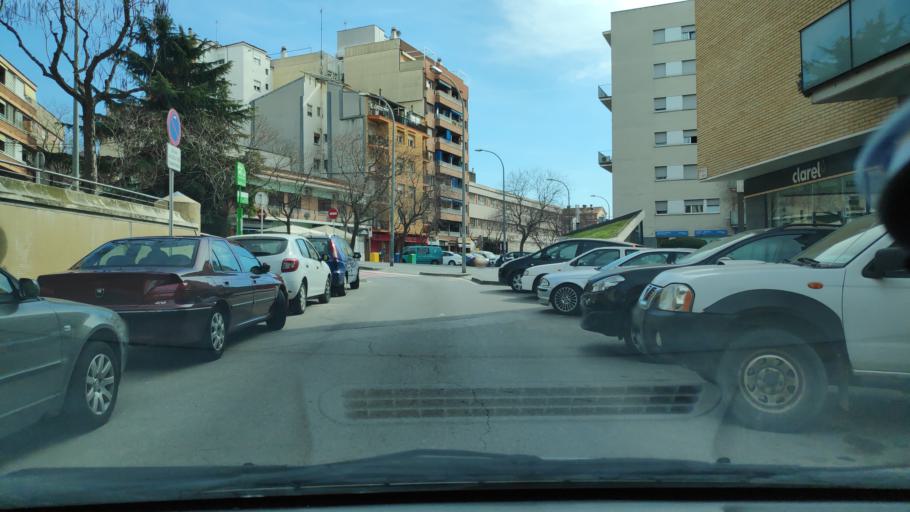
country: ES
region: Catalonia
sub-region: Provincia de Barcelona
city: Rubi
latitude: 41.4964
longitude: 2.0315
